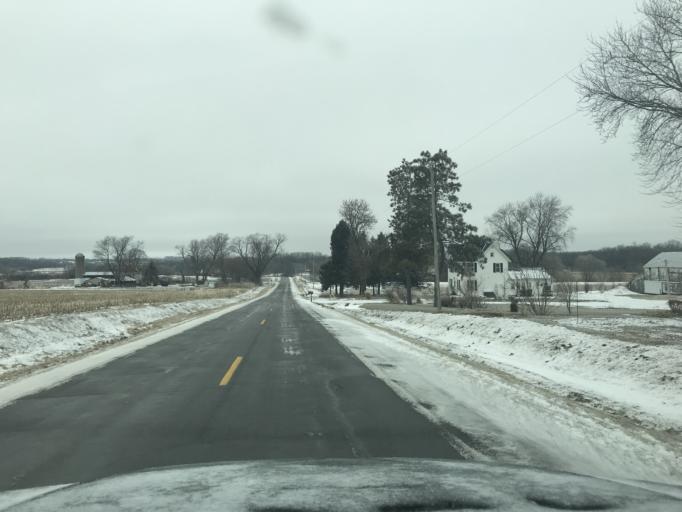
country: US
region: Wisconsin
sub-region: Dane County
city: Cottage Grove
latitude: 43.1039
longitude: -89.2357
